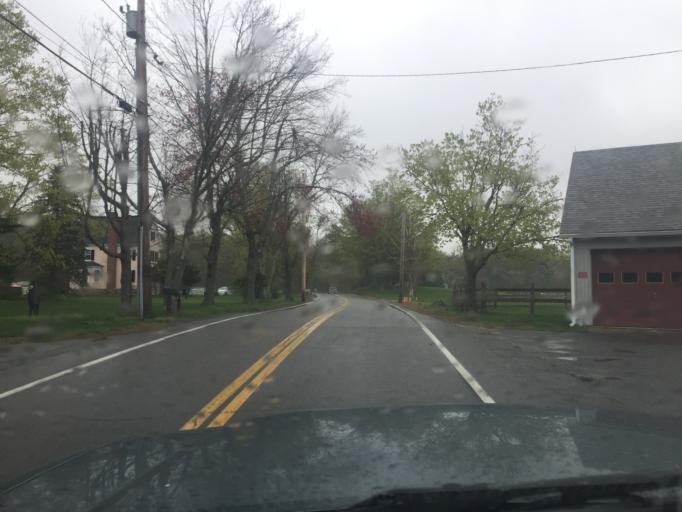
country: US
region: Massachusetts
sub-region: Norfolk County
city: Dover
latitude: 42.2255
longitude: -71.2606
